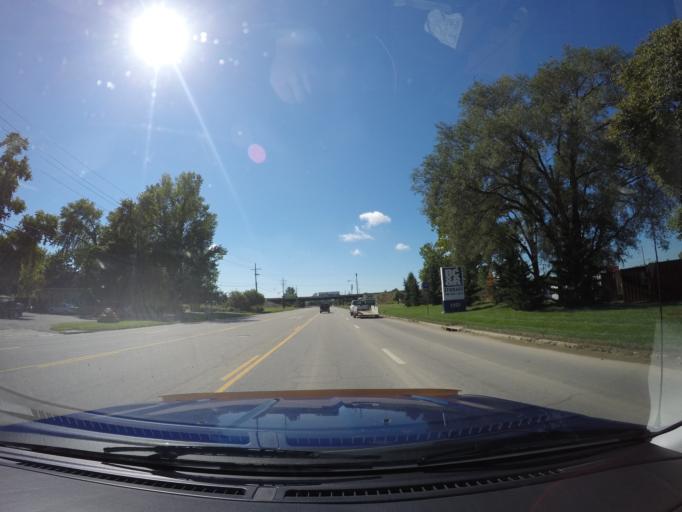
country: US
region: Kansas
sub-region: Douglas County
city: Lawrence
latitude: 38.9950
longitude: -95.2334
